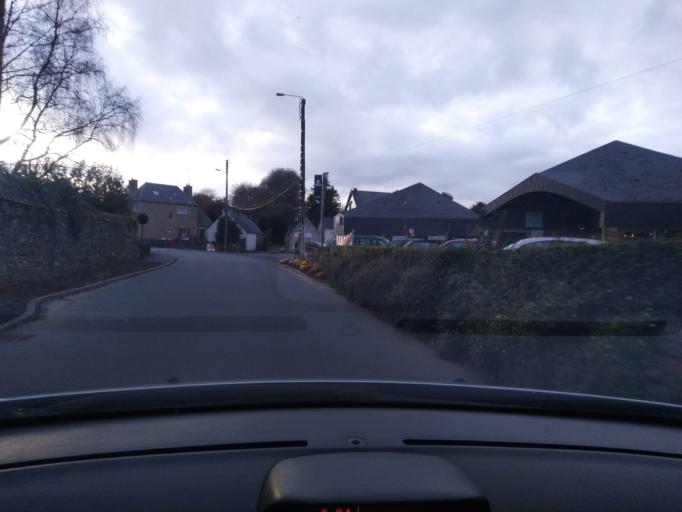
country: FR
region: Brittany
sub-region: Departement des Cotes-d'Armor
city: Plouaret
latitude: 48.6116
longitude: -3.4739
